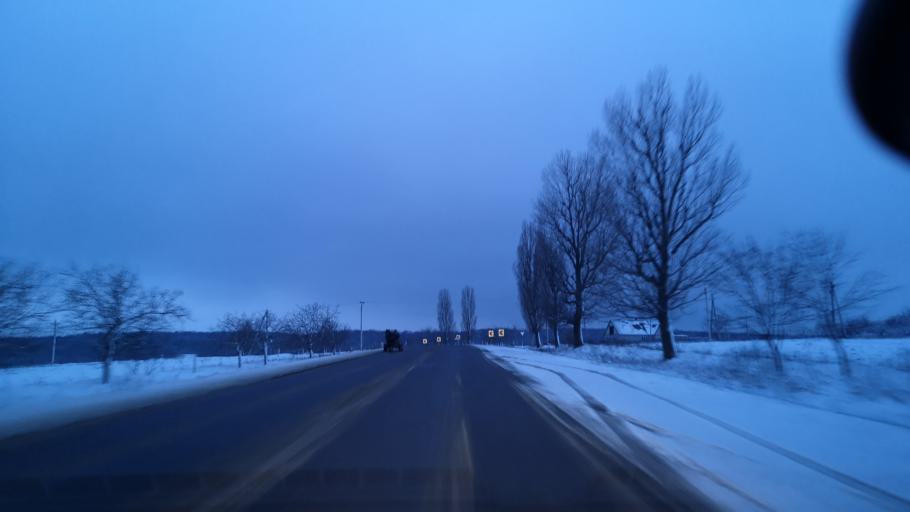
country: MD
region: Rezina
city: Rezina
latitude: 47.7360
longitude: 28.8801
